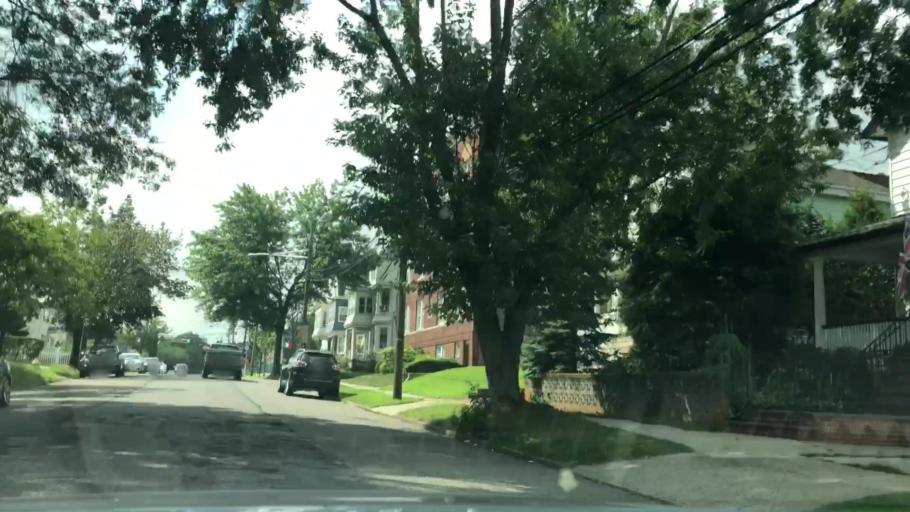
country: US
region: New Jersey
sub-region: Essex County
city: Bloomfield
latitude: 40.7902
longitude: -74.1859
